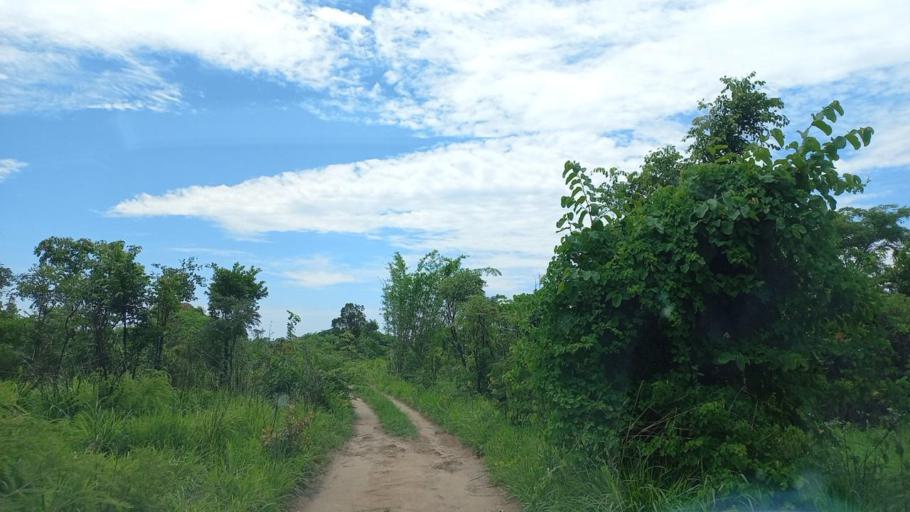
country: ZM
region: Copperbelt
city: Kitwe
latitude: -12.7905
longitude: 28.3984
